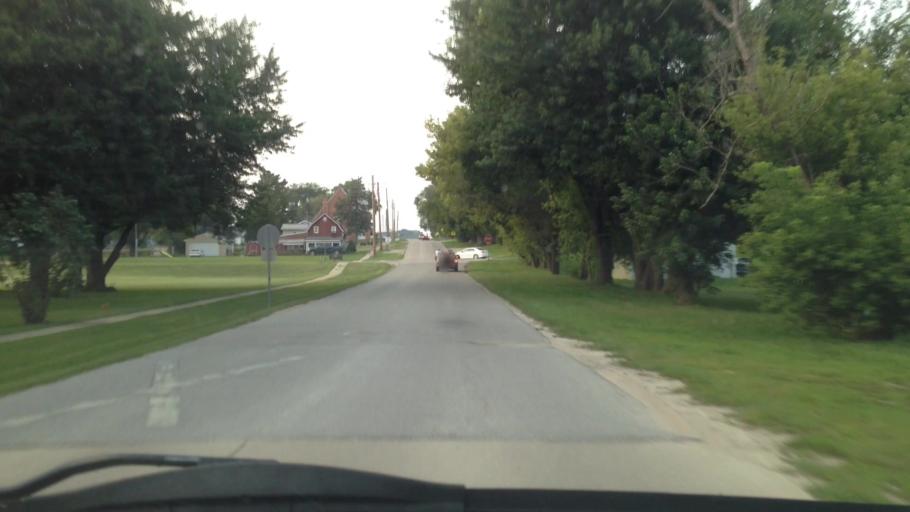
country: US
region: Iowa
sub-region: Linn County
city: Palo
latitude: 42.0935
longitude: -91.8734
